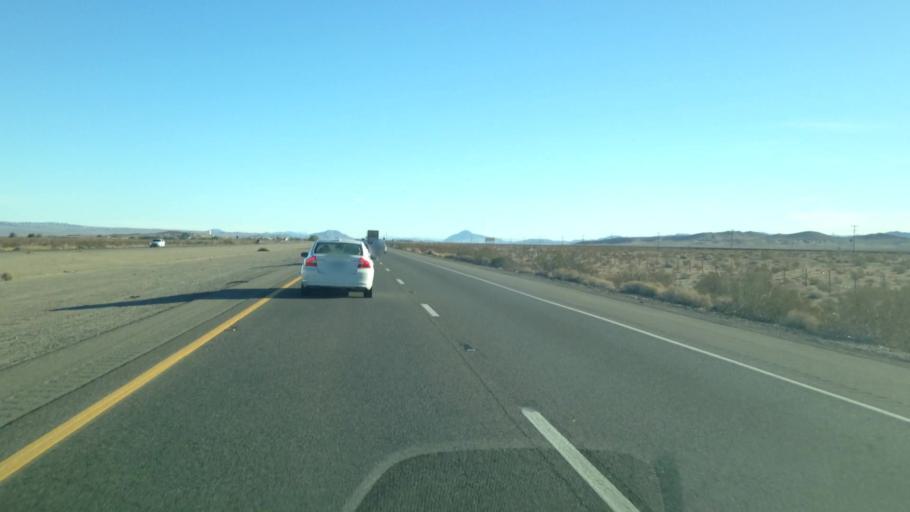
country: US
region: California
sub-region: San Bernardino County
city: Barstow
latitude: 34.9342
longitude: -116.7092
